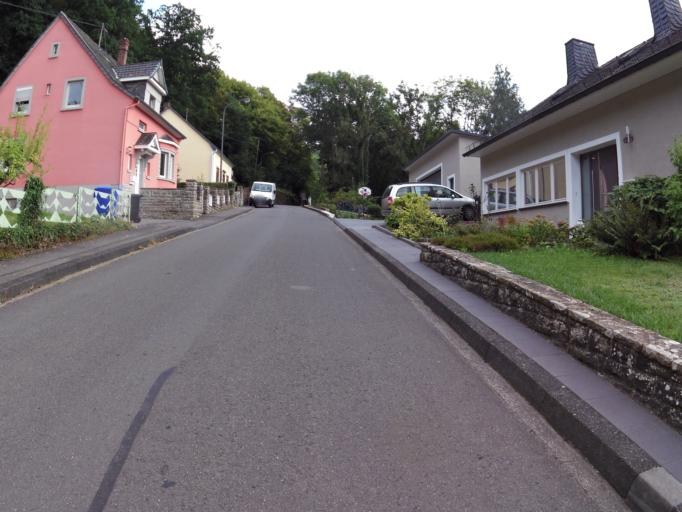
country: DE
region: Rheinland-Pfalz
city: Kyllburg
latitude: 50.0378
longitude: 6.5923
